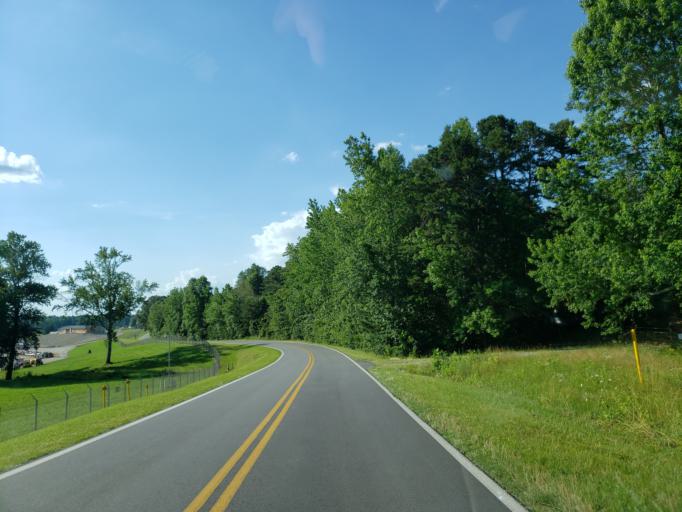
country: US
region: Georgia
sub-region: Haralson County
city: Bremen
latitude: 33.6973
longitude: -85.1359
